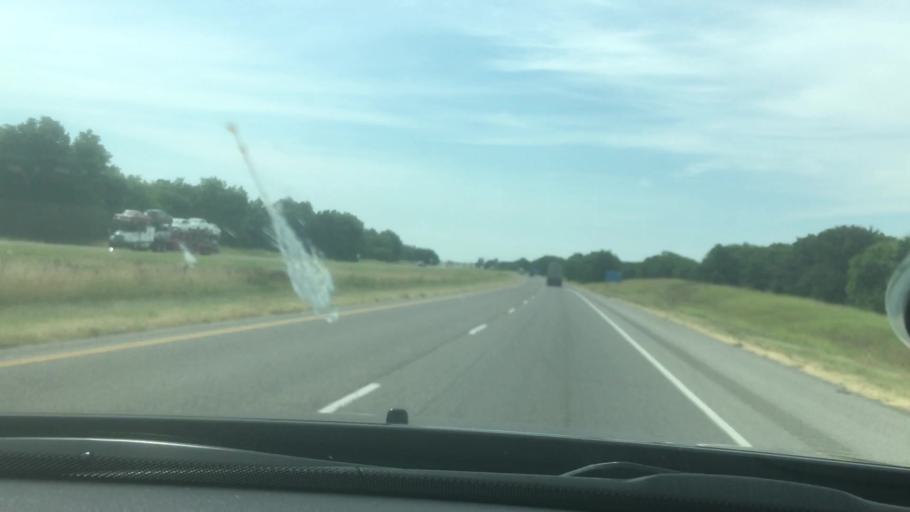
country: US
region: Oklahoma
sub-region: Murray County
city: Davis
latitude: 34.5226
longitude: -97.1844
